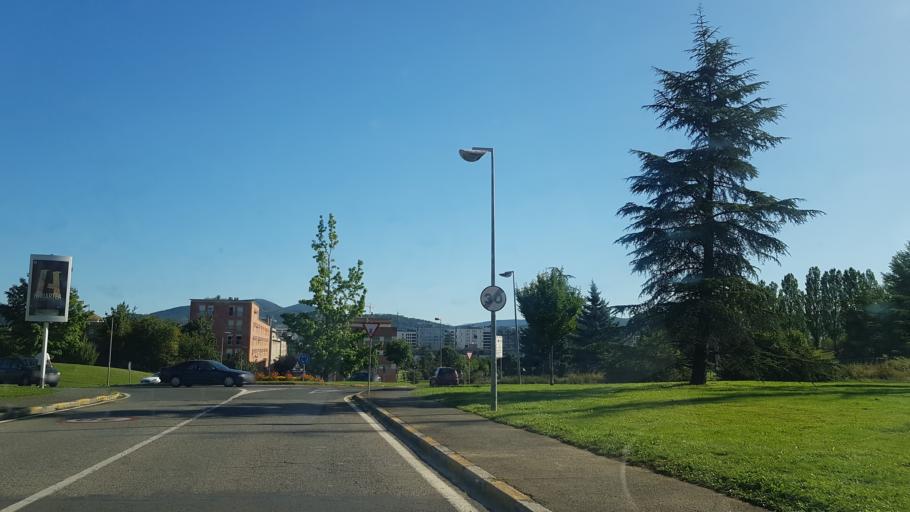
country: ES
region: Navarre
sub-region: Provincia de Navarra
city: Burlata
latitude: 42.8092
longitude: -1.6117
